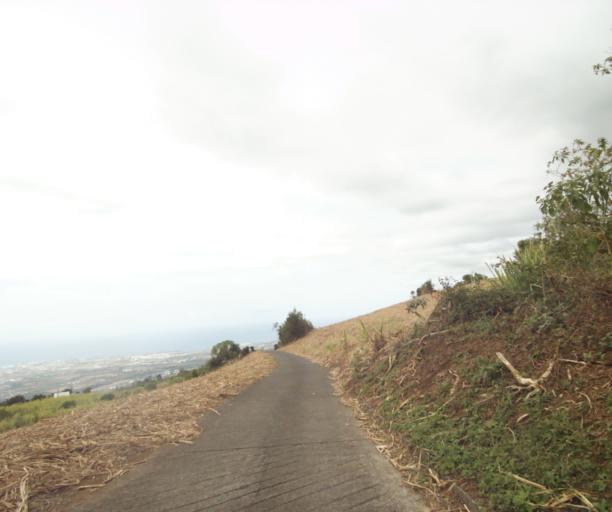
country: RE
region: Reunion
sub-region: Reunion
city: Saint-Paul
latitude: -21.0205
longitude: 55.3252
